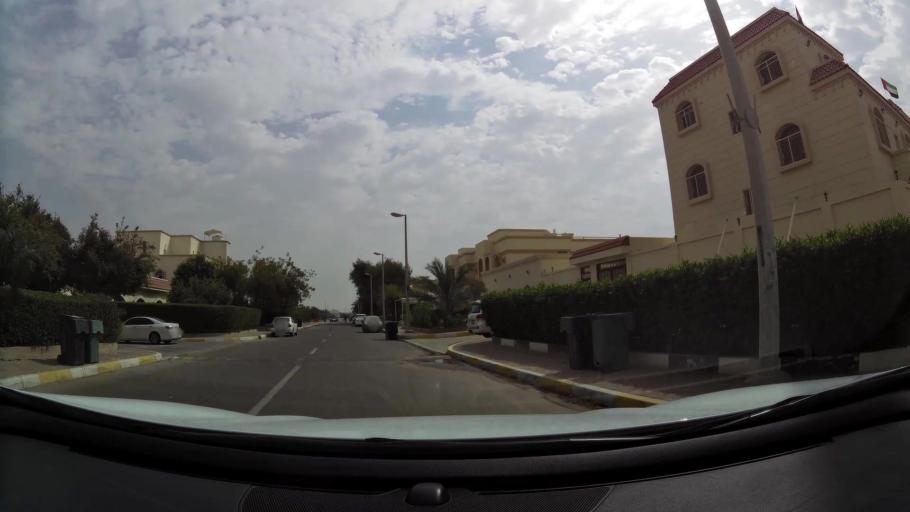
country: AE
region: Abu Dhabi
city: Abu Dhabi
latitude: 24.3201
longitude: 54.6346
